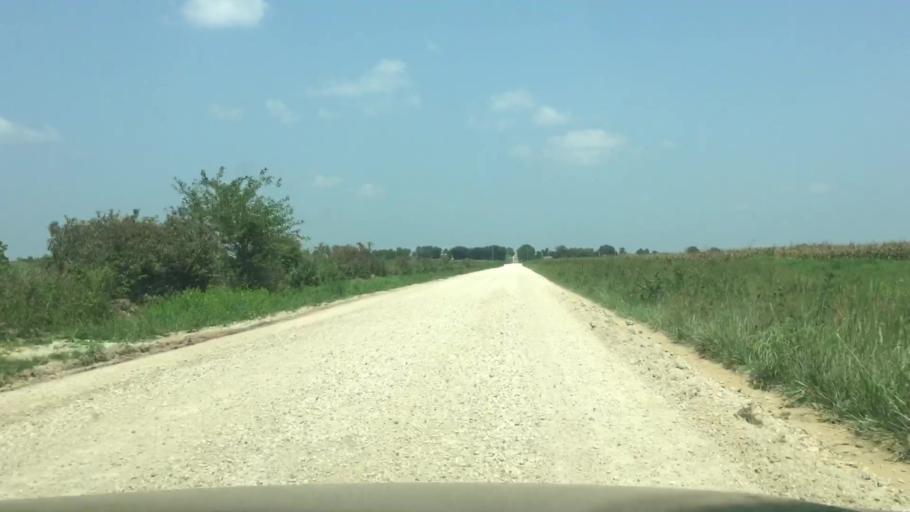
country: US
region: Kansas
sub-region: Allen County
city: Iola
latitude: 37.8713
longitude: -95.3911
